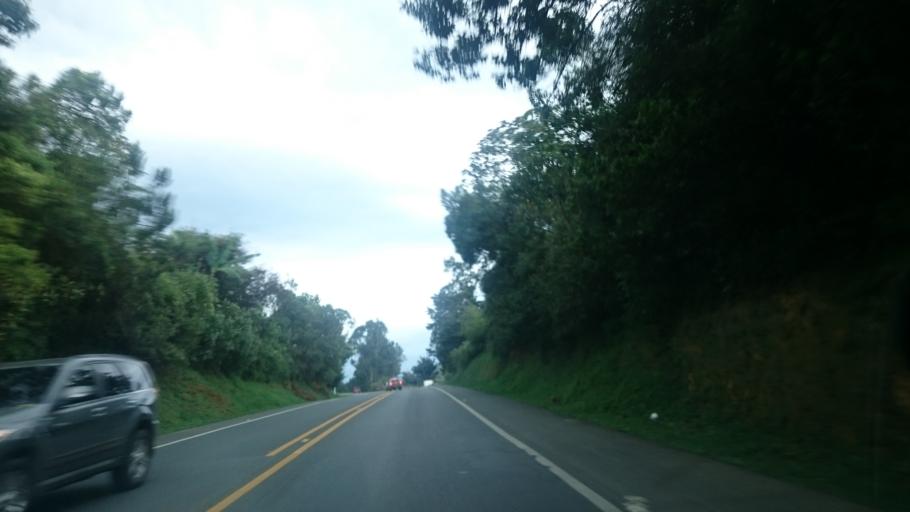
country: CO
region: Cauca
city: Cajibio
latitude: 2.5899
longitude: -76.5319
